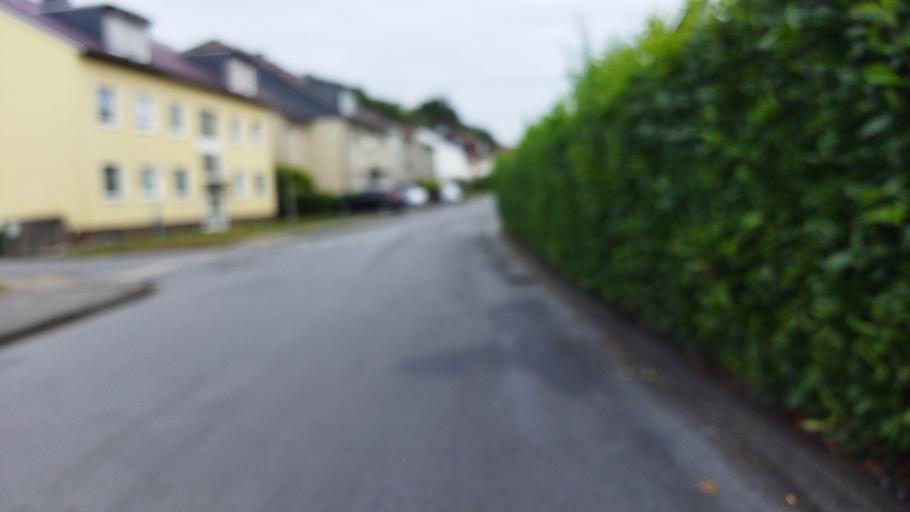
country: DE
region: Lower Saxony
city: Bad Rothenfelde
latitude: 52.1049
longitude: 8.1607
